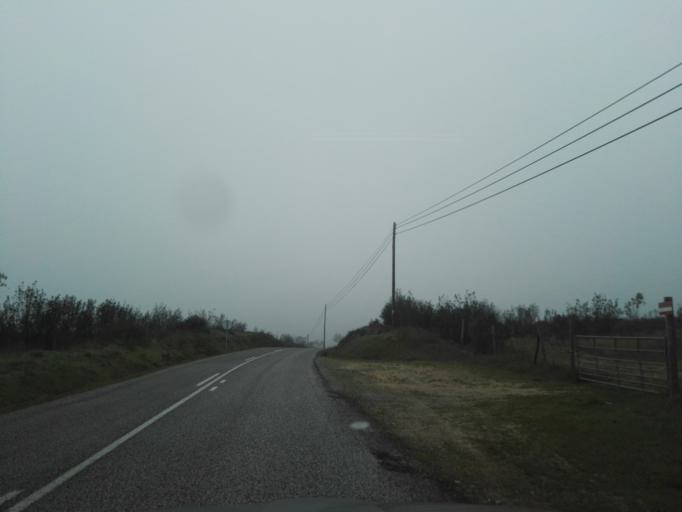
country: PT
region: Evora
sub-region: Montemor-O-Novo
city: Montemor-o-Novo
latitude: 38.7819
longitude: -8.2178
